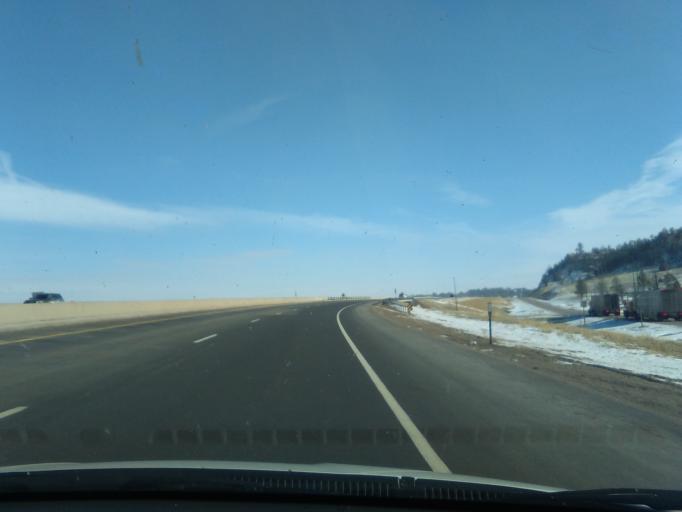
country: US
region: Wyoming
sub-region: Laramie County
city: Pine Bluffs
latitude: 41.1755
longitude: -104.0776
